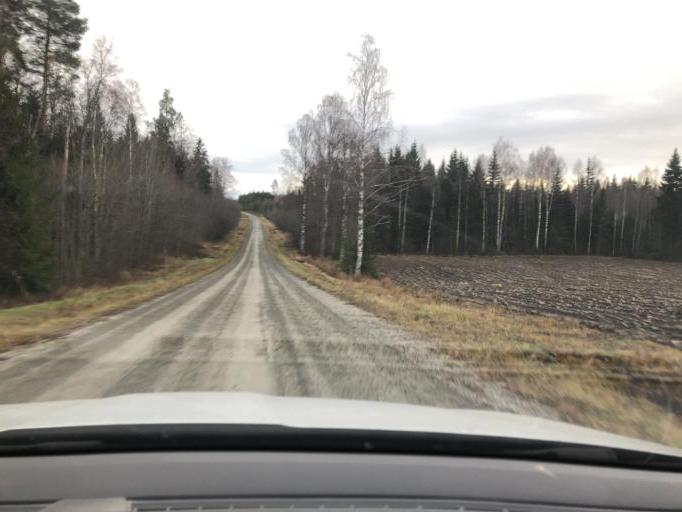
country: SE
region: Gaevleborg
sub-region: Hudiksvalls Kommun
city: Sorforsa
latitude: 61.6530
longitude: 16.9273
